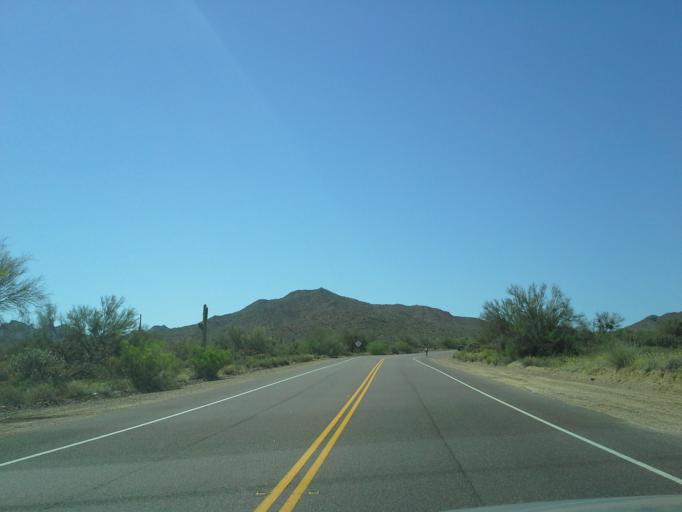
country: US
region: Arizona
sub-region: Maricopa County
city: Fountain Hills
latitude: 33.5384
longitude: -111.6103
